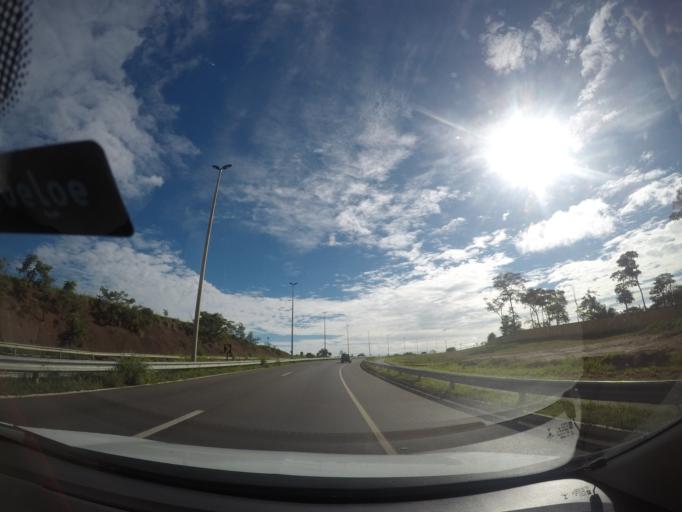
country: BR
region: Goias
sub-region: Senador Canedo
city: Senador Canedo
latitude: -16.6869
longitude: -49.1642
